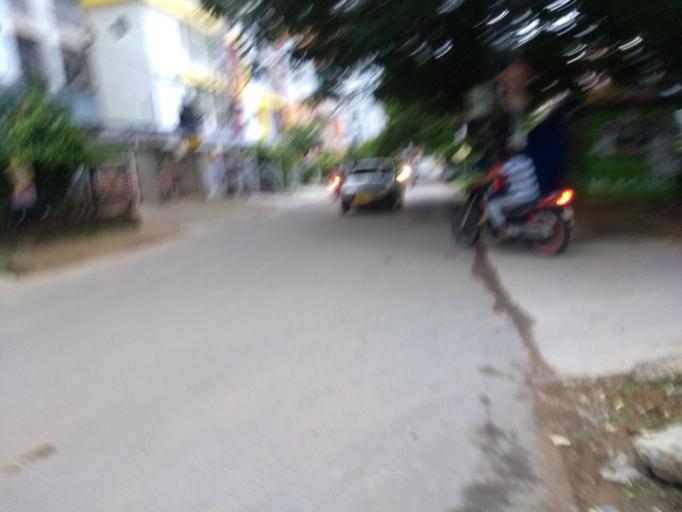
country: IN
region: Telangana
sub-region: Rangareddi
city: Kukatpalli
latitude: 17.4886
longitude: 78.3853
